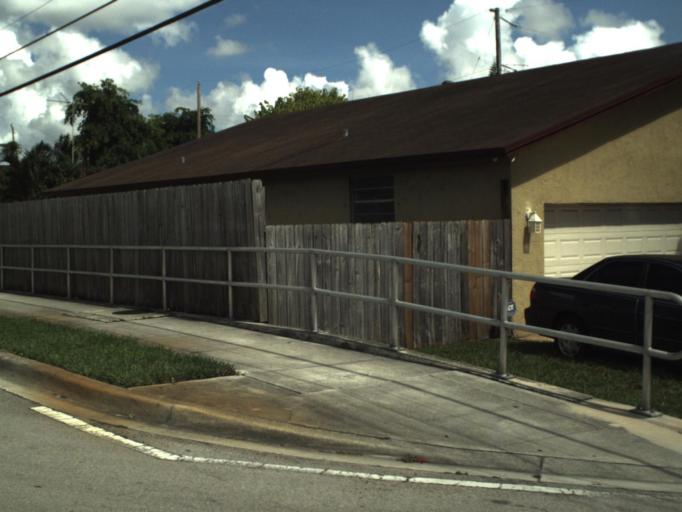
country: US
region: Florida
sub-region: Broward County
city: Miramar
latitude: 25.9938
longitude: -80.2723
